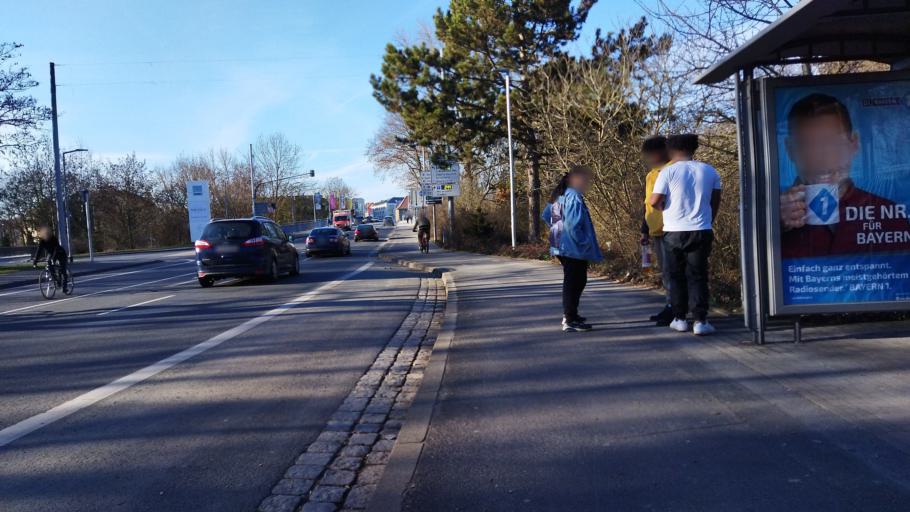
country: DE
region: Bavaria
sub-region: Regierungsbezirk Unterfranken
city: Sennfeld
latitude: 50.0408
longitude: 10.2400
